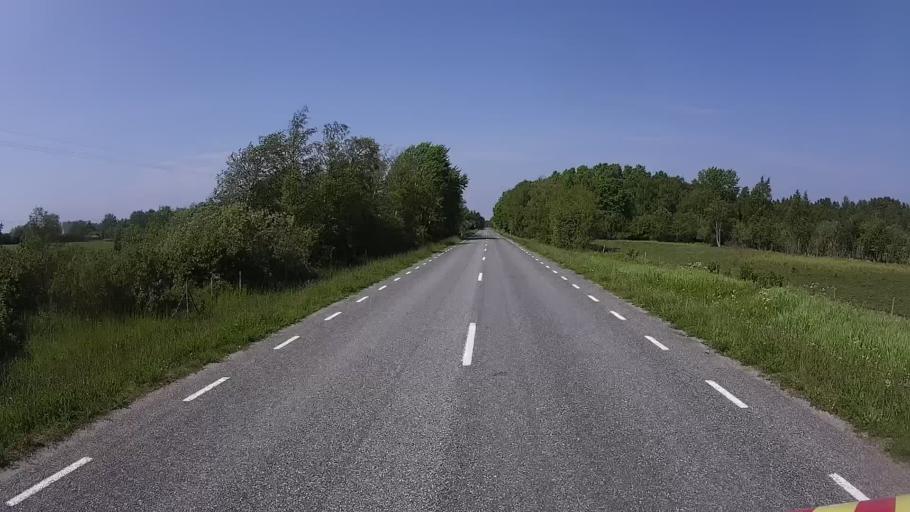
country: EE
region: Saare
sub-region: Kuressaare linn
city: Kuressaare
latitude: 58.3711
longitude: 22.0457
